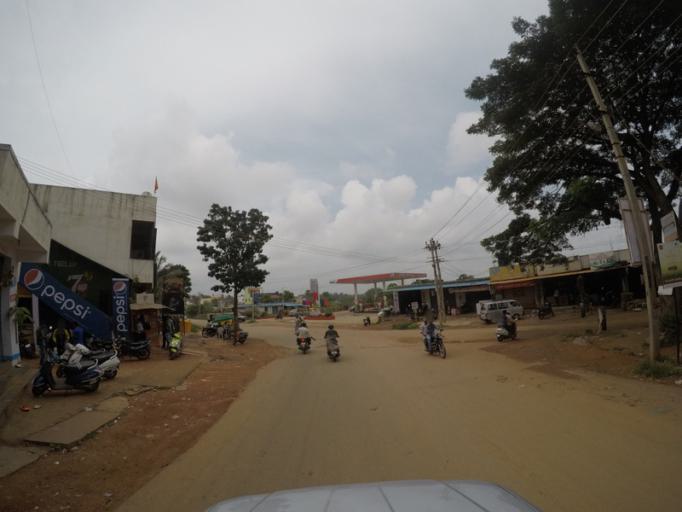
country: IN
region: Karnataka
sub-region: Bangalore Urban
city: Yelahanka
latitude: 13.1105
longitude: 77.5279
